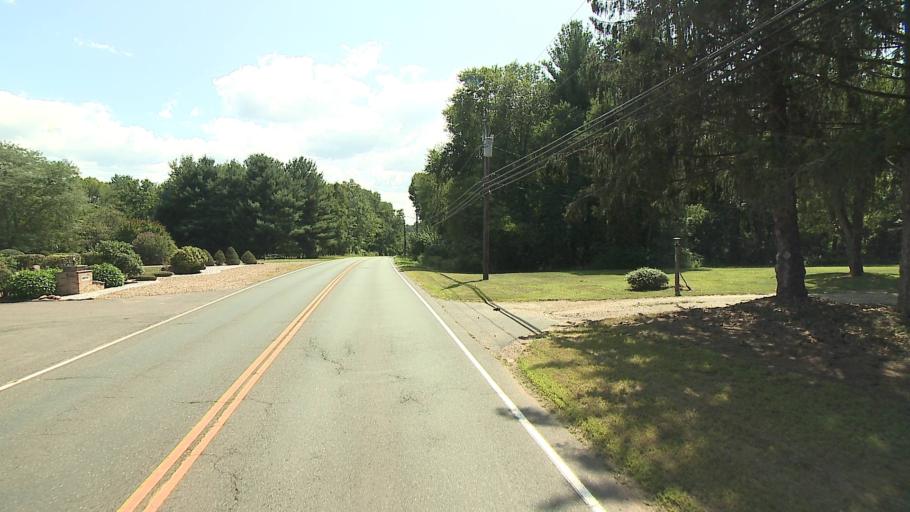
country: US
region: Connecticut
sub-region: Hartford County
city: Broad Brook
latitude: 41.9301
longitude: -72.5541
